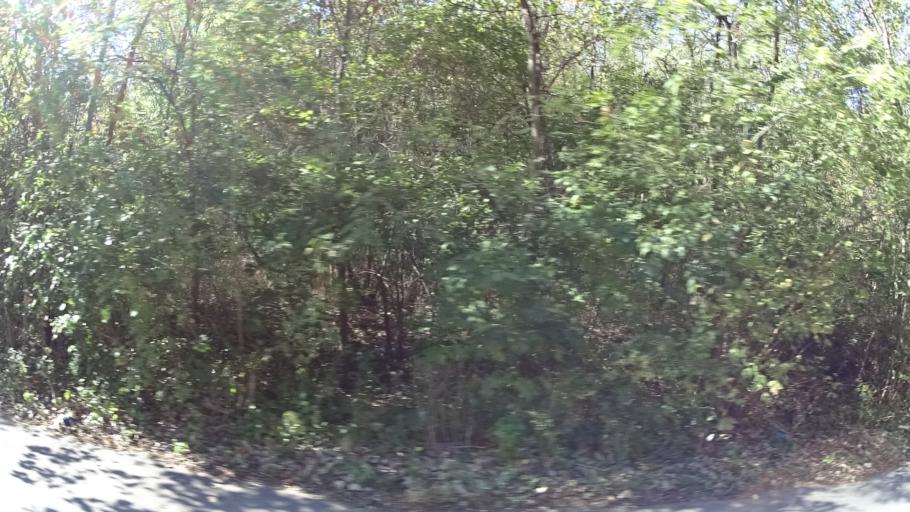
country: US
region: Ohio
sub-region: Lorain County
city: Lorain
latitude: 41.4358
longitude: -82.1698
